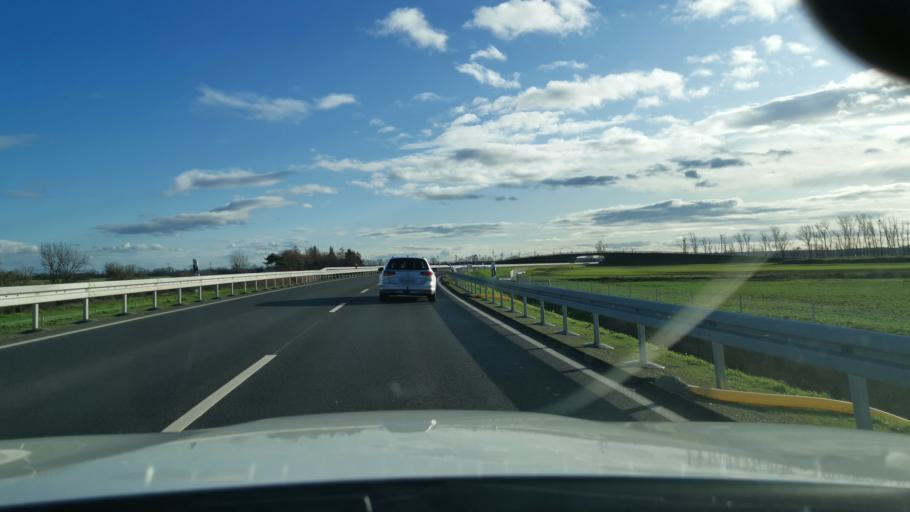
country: DE
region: Saxony-Anhalt
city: Wittenburg
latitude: 51.8240
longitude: 12.6435
